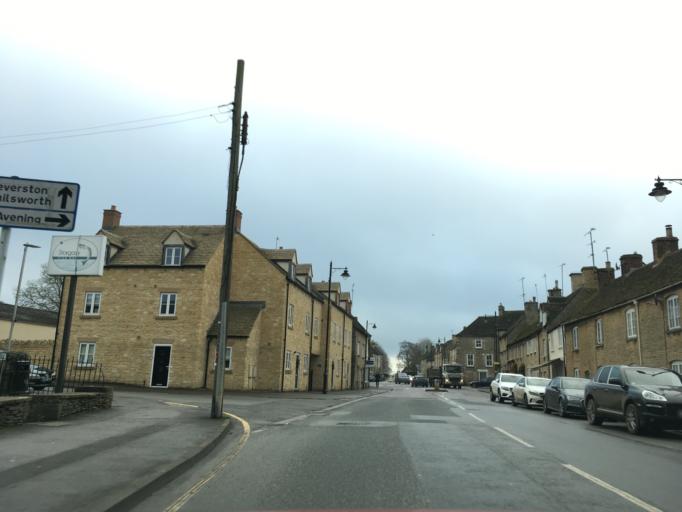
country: GB
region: England
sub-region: Gloucestershire
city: Tetbury
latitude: 51.6398
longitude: -2.1613
